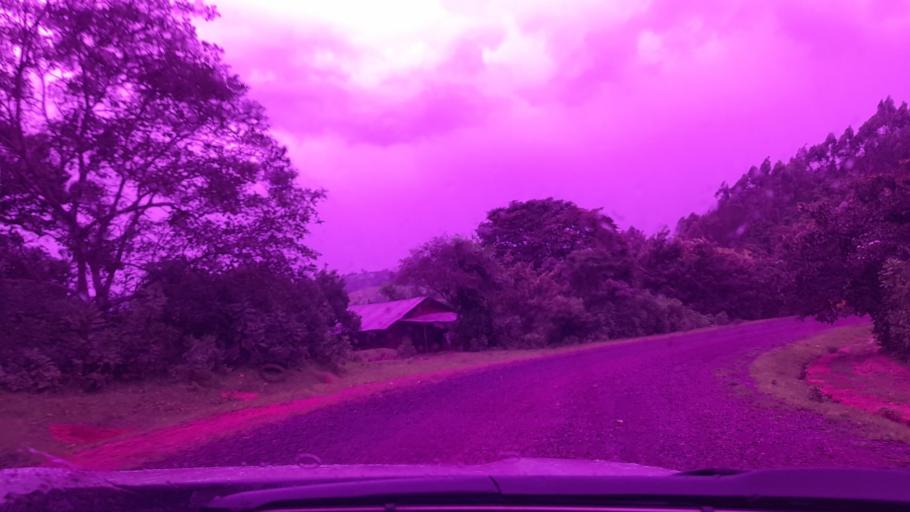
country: ET
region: Oromiya
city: Metu
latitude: 8.4368
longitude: 35.6150
